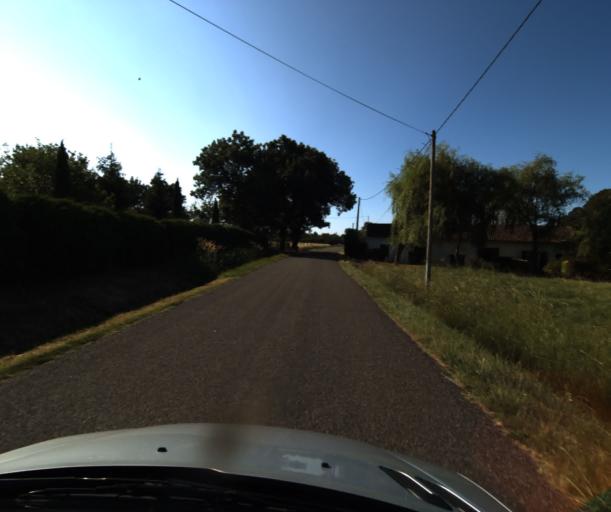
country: FR
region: Midi-Pyrenees
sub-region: Departement du Tarn-et-Garonne
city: Saint-Porquier
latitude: 44.0561
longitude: 1.2097
